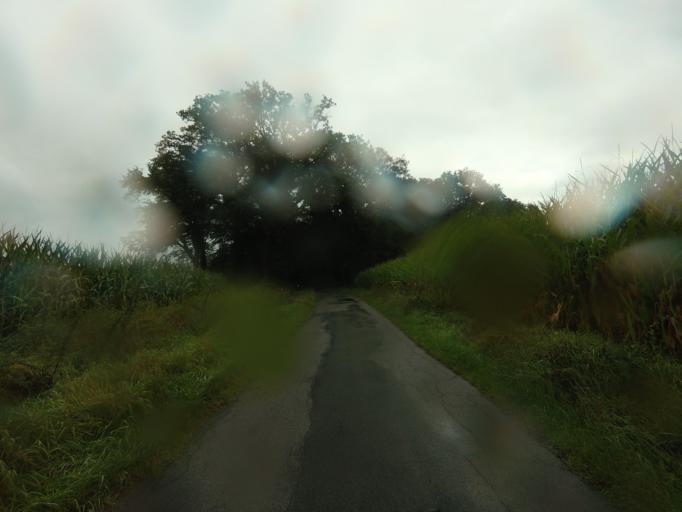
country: DE
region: North Rhine-Westphalia
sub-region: Regierungsbezirk Munster
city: Gronau
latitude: 52.1879
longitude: 7.0066
